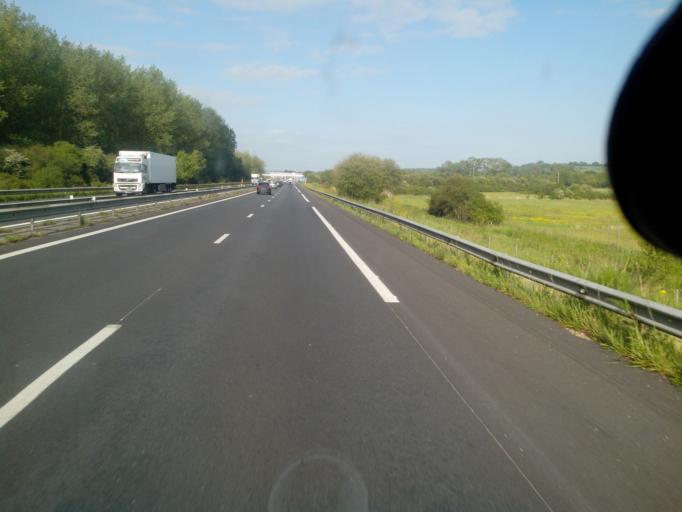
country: FR
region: Lower Normandy
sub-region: Departement du Calvados
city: Dozule
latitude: 49.2254
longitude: -0.0947
